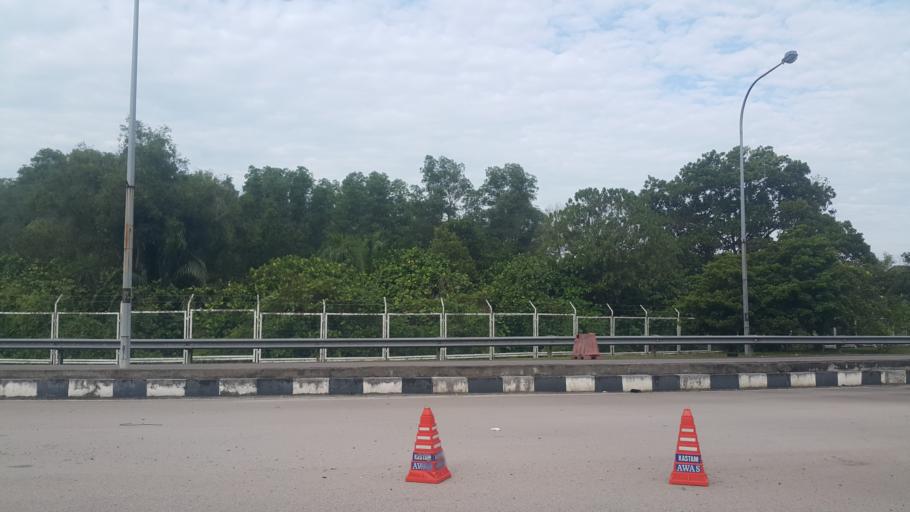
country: MY
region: Johor
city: Pekan Nenas
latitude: 1.3774
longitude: 103.5967
